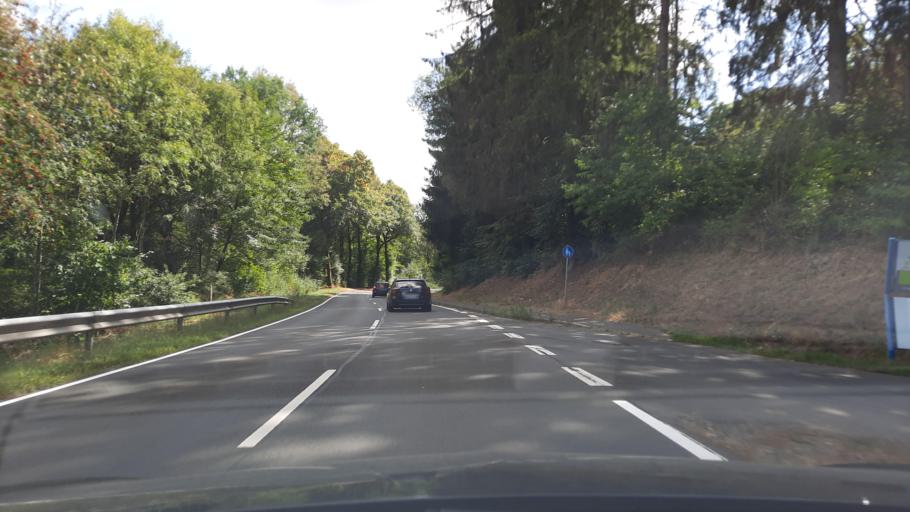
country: DE
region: Rheinland-Pfalz
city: Prum
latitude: 50.2141
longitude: 6.4142
